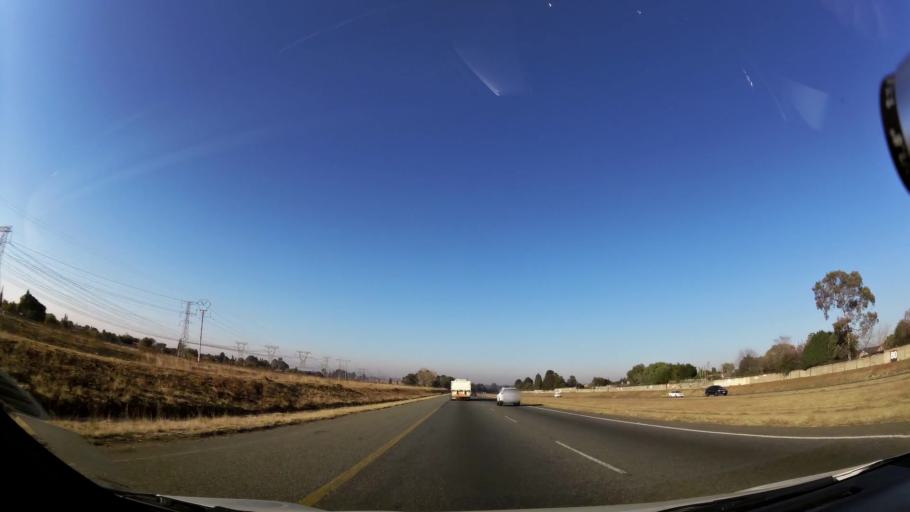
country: ZA
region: Gauteng
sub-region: Ekurhuleni Metropolitan Municipality
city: Germiston
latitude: -26.3203
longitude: 28.1127
